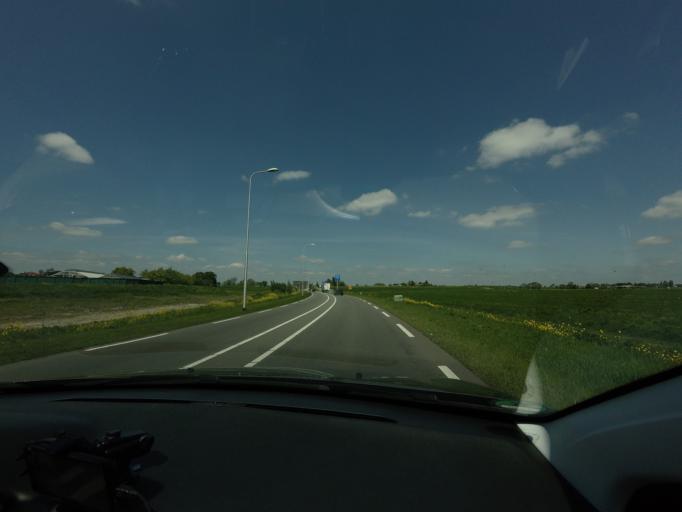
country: NL
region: North Holland
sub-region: Gemeente Uithoorn
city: Uithoorn
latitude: 52.2387
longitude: 4.8554
